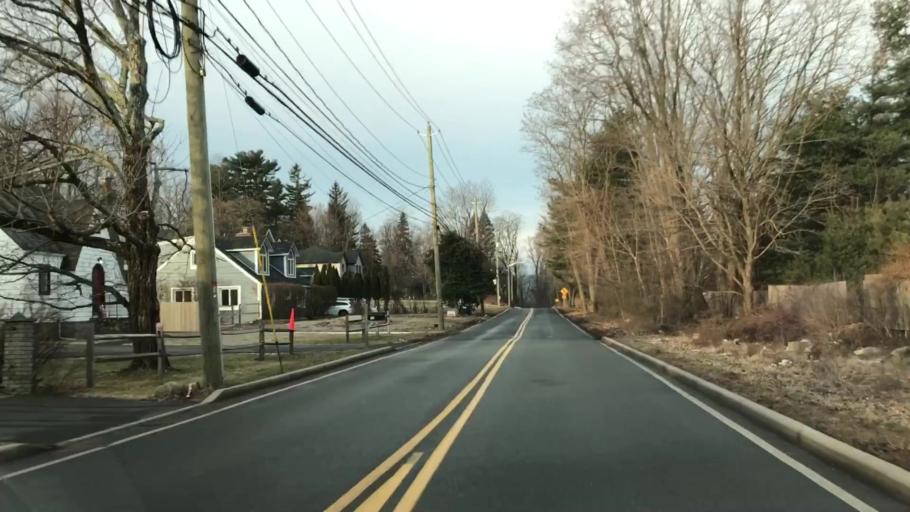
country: US
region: New York
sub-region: Rockland County
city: Viola
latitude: 41.1365
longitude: -74.0846
